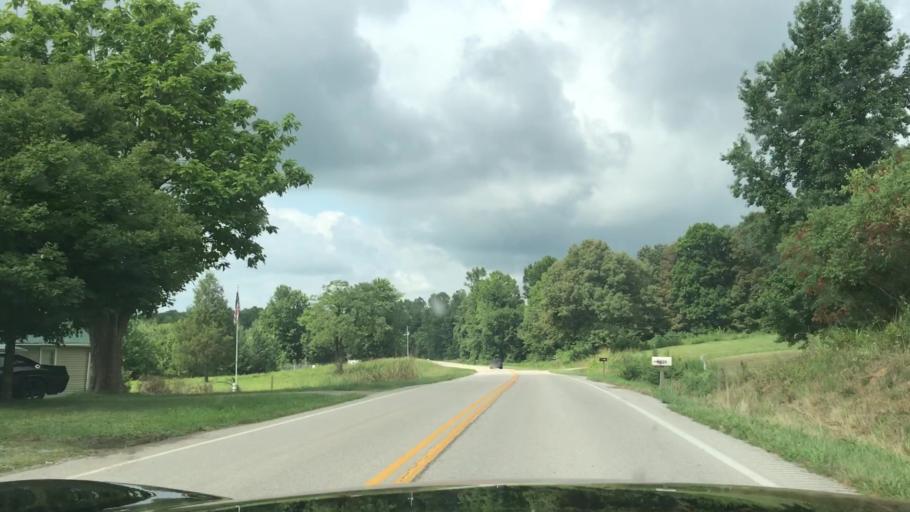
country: US
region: Kentucky
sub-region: Butler County
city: Morgantown
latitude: 37.1981
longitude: -86.7411
